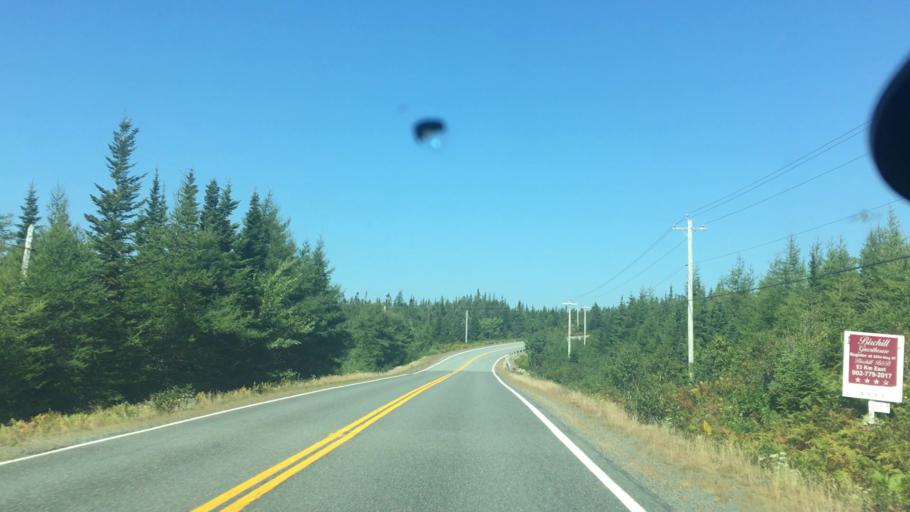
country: CA
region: Nova Scotia
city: Antigonish
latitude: 45.0067
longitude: -62.1047
